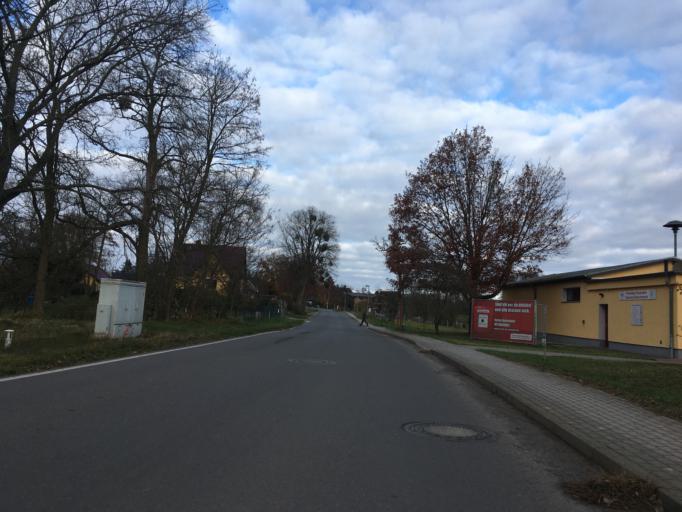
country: DE
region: Brandenburg
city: Muncheberg
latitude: 52.5421
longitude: 14.1692
